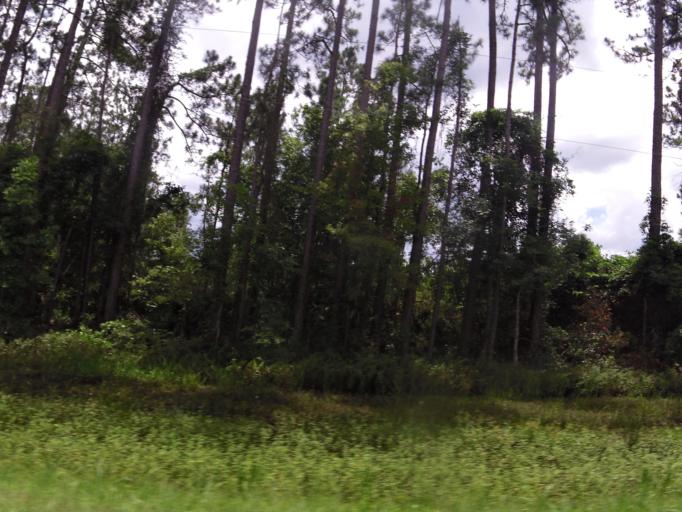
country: US
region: Florida
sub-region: Saint Johns County
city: Saint Augustine Shores
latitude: 29.6535
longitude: -81.3590
